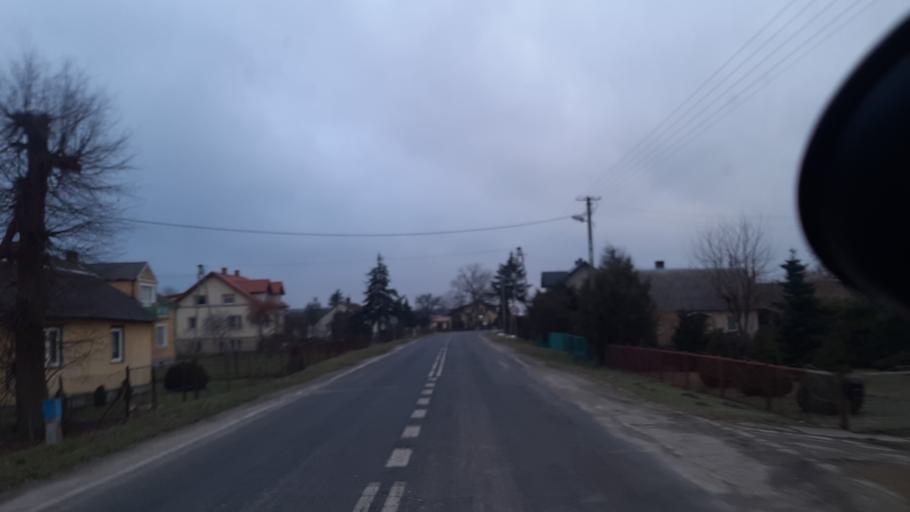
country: PL
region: Lublin Voivodeship
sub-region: Powiat parczewski
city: Debowa Kloda
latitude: 51.6208
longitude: 23.0887
